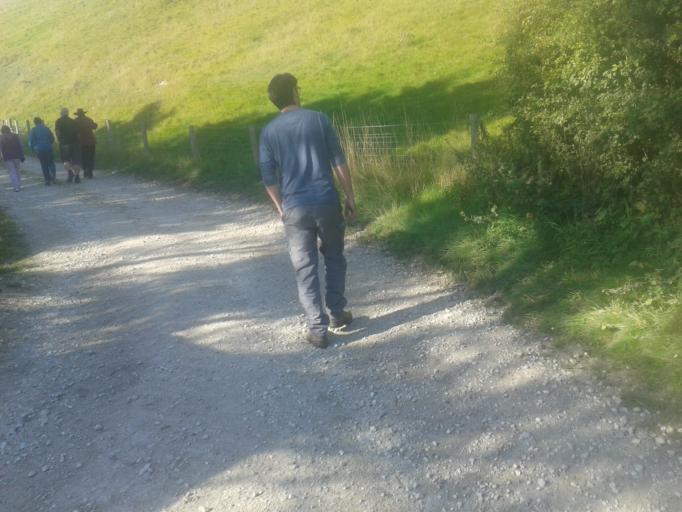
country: GB
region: England
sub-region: North Yorkshire
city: Thixendale
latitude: 54.0397
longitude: -0.7180
